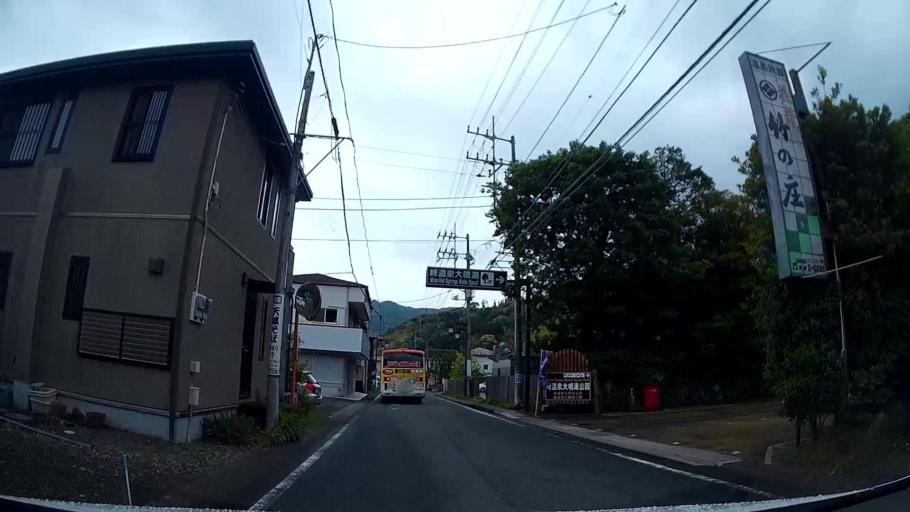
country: JP
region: Shizuoka
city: Shimoda
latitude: 34.7576
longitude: 138.9833
